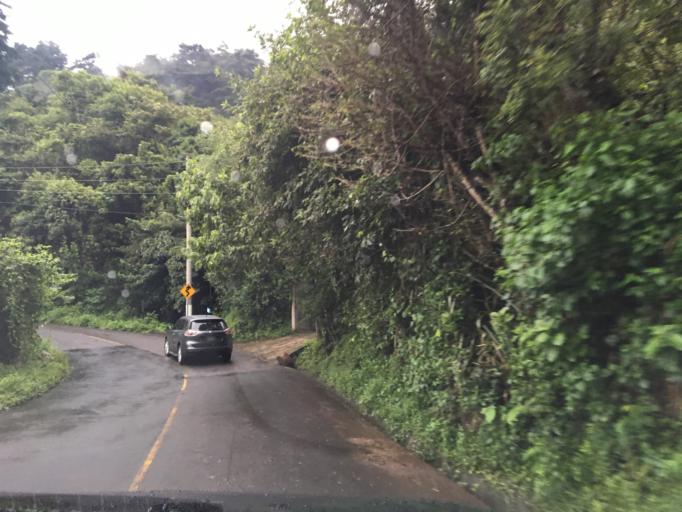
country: GT
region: Guatemala
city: Santa Catarina Pinula
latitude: 14.5457
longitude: -90.4985
